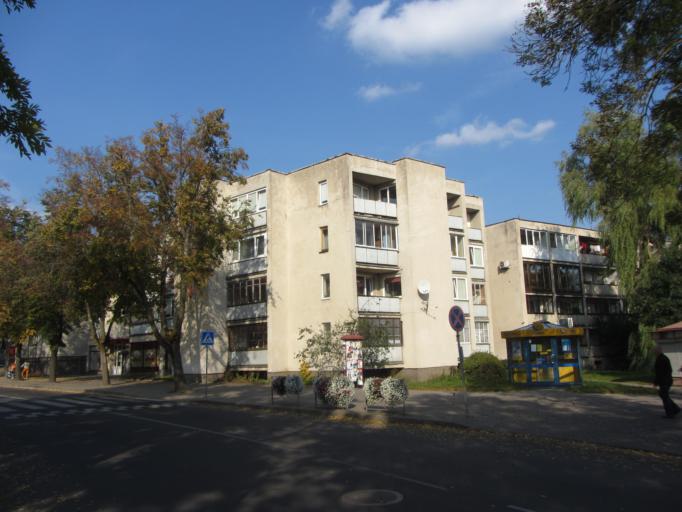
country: LT
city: Trakai
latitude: 54.6382
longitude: 24.9340
